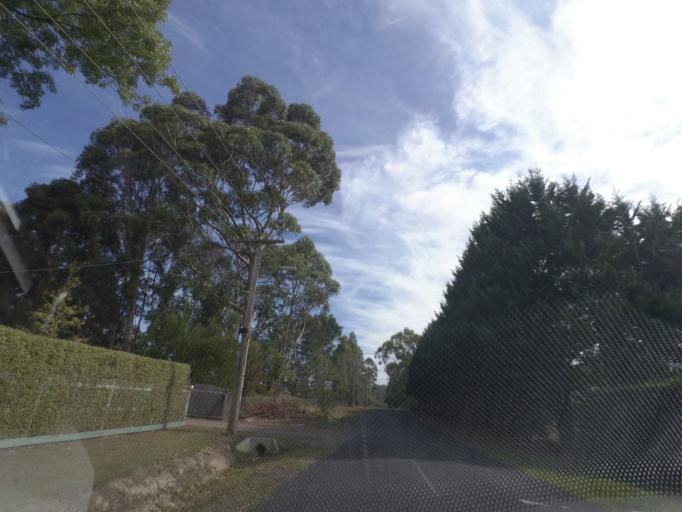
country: AU
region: Victoria
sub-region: Yarra Ranges
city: Healesville
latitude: -37.6434
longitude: 145.5331
